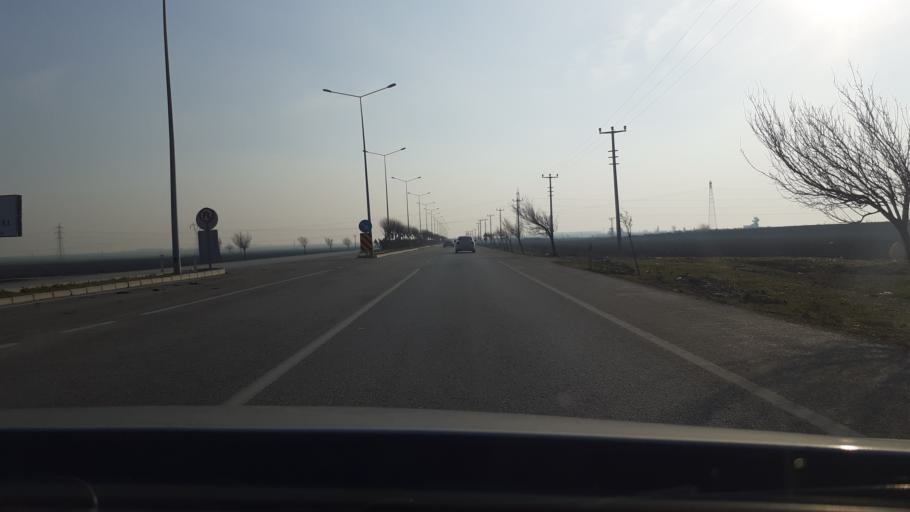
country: TR
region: Hatay
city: Serinyol
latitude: 36.3715
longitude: 36.2404
